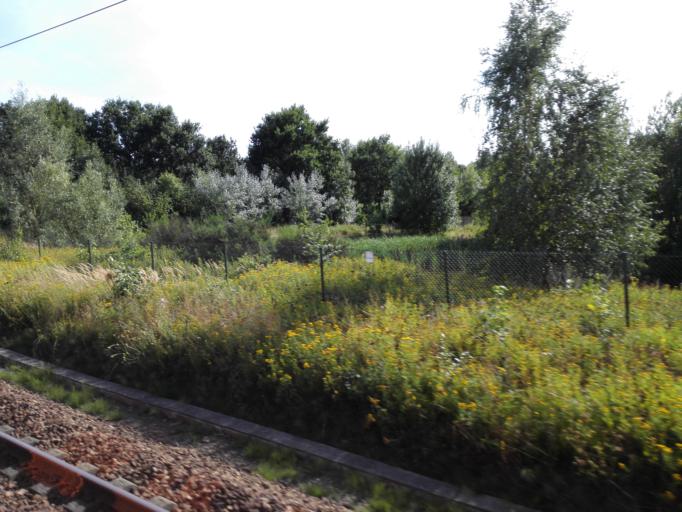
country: BE
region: Flanders
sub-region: Provincie Vlaams-Brabant
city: Haacht
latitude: 50.9533
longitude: 4.6473
